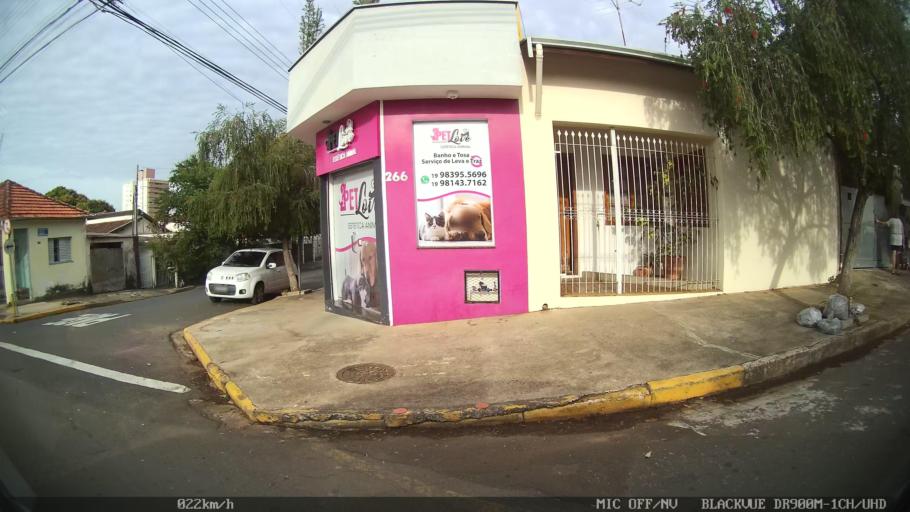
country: BR
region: Sao Paulo
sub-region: Piracicaba
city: Piracicaba
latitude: -22.7305
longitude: -47.6335
